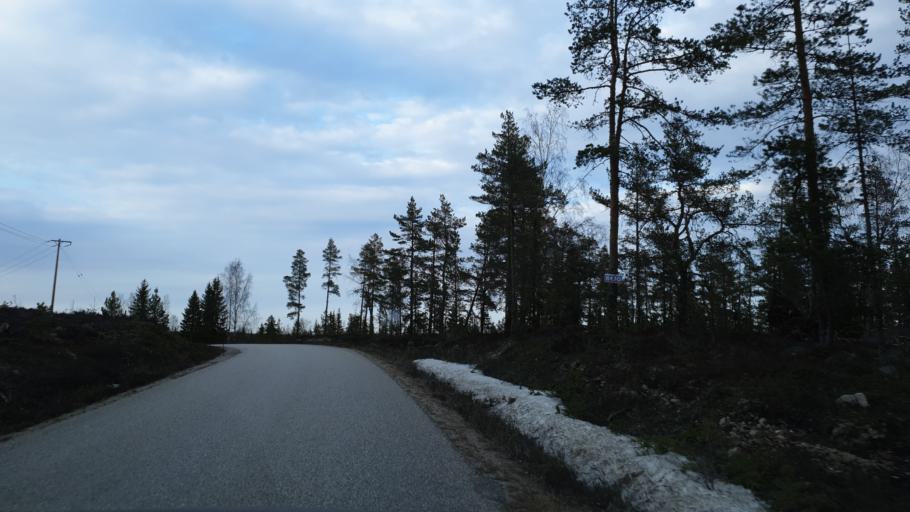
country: SE
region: Vaesternorrland
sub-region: Sundsvalls Kommun
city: Njurundabommen
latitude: 62.0114
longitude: 17.4000
